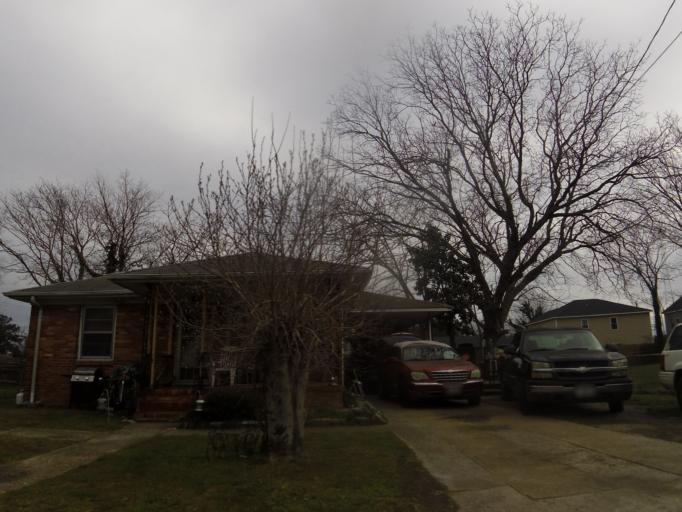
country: US
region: Virginia
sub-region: City of Portsmouth
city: Portsmouth Heights
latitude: 36.8234
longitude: -76.3406
